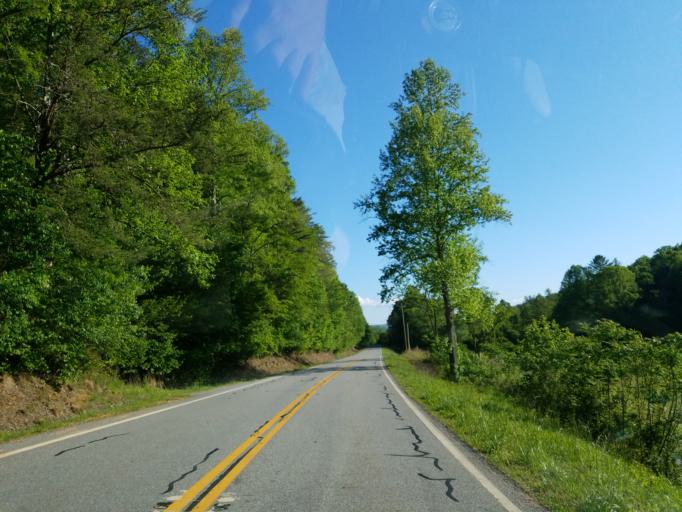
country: US
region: Georgia
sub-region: Fannin County
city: Blue Ridge
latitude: 34.7871
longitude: -84.1839
